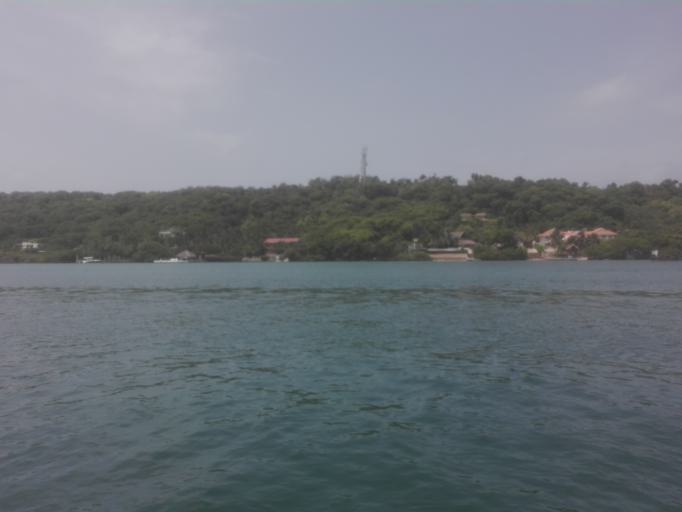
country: CO
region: Bolivar
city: Turbana
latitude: 10.1611
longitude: -75.6713
